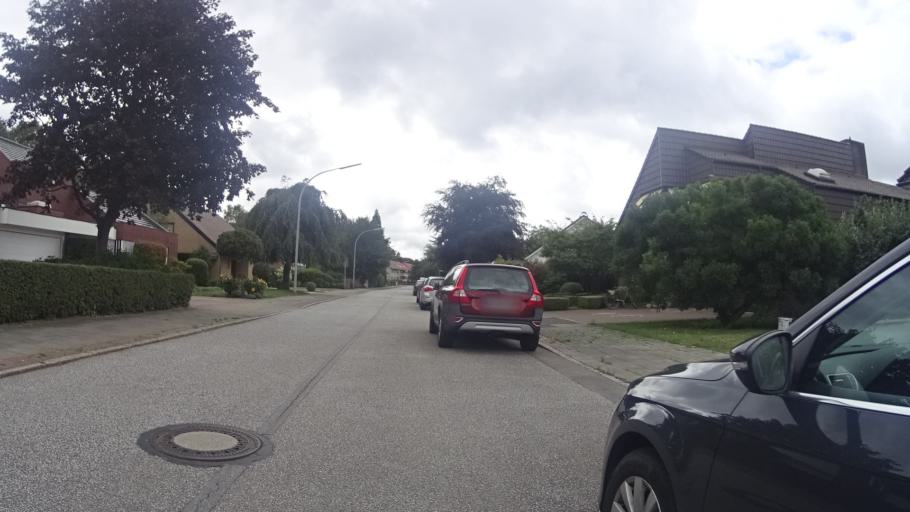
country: DE
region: Bremen
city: Bremerhaven
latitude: 53.5337
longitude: 8.6107
